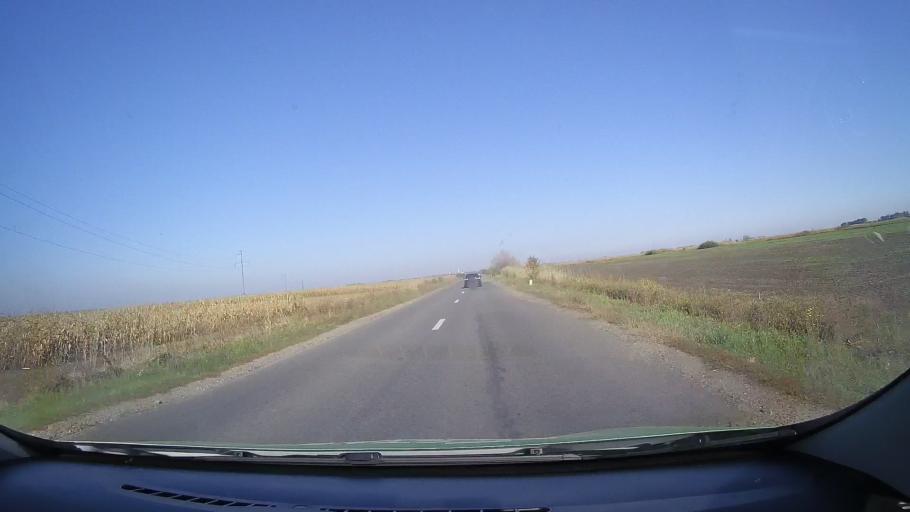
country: RO
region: Satu Mare
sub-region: Comuna Cauas
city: Cauas
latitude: 47.6088
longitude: 22.5404
